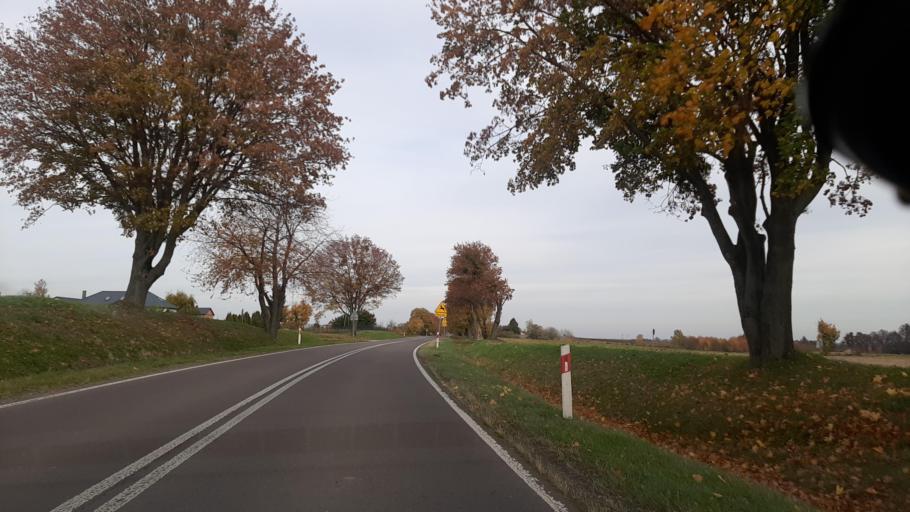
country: PL
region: Lublin Voivodeship
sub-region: Powiat pulawski
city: Markuszow
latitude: 51.3368
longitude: 22.2547
